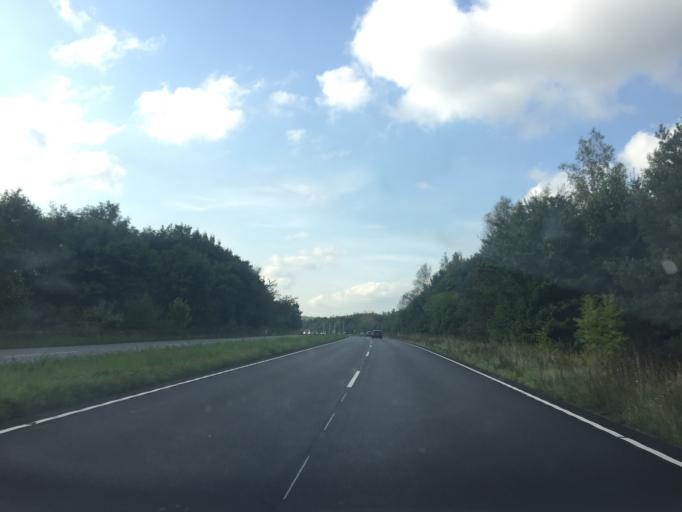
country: DK
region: Zealand
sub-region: Holbaek Kommune
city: Jyderup
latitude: 55.6591
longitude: 11.4220
